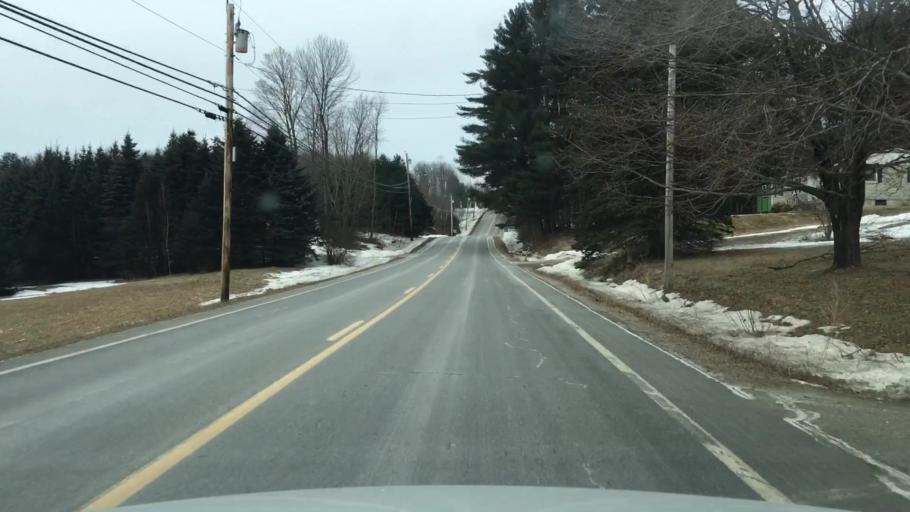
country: US
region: Maine
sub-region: Lincoln County
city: Whitefield
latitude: 44.2268
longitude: -69.6095
